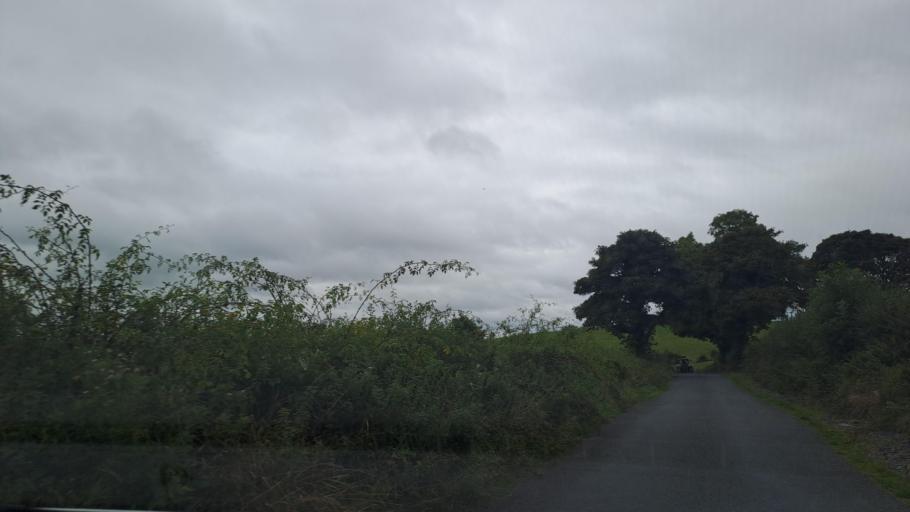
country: IE
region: Ulster
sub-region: An Cabhan
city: Bailieborough
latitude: 54.0086
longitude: -6.8907
